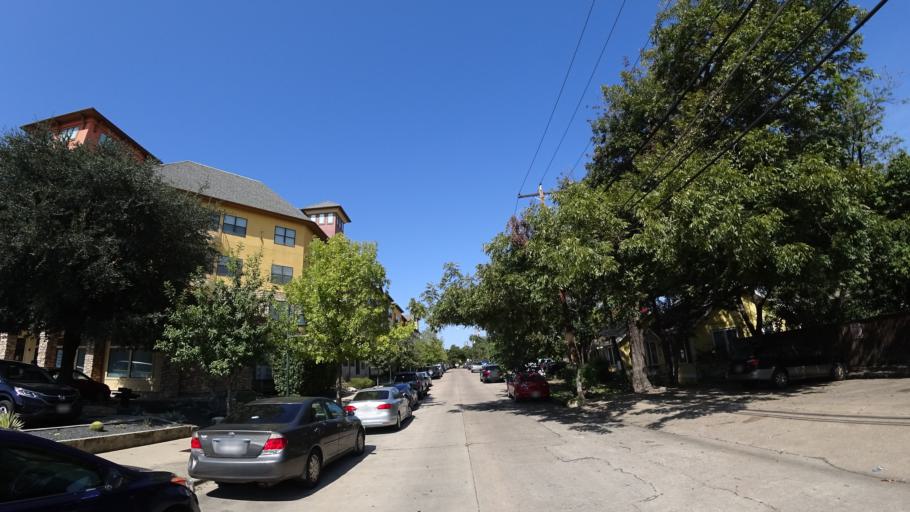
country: US
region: Texas
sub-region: Travis County
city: Austin
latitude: 30.2928
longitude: -97.7411
